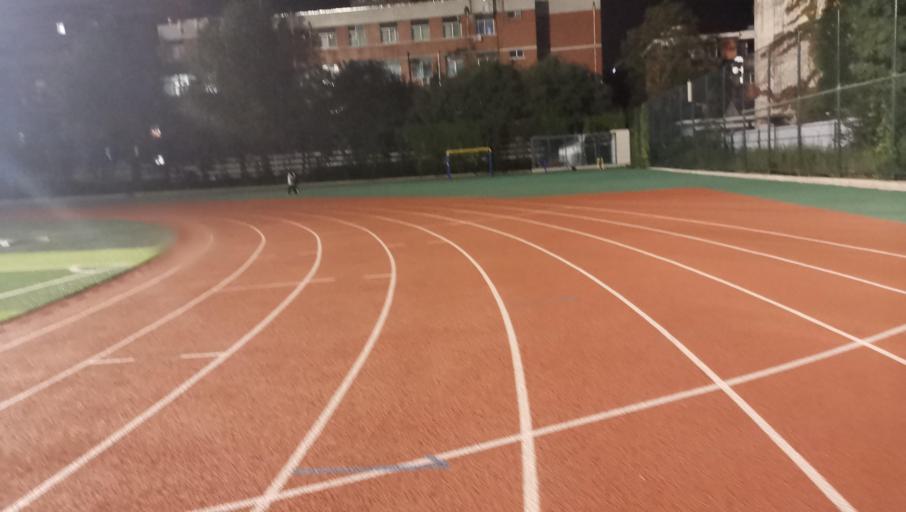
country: CN
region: Shandong Sheng
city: Jinan
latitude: 36.6501
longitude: 117.0123
